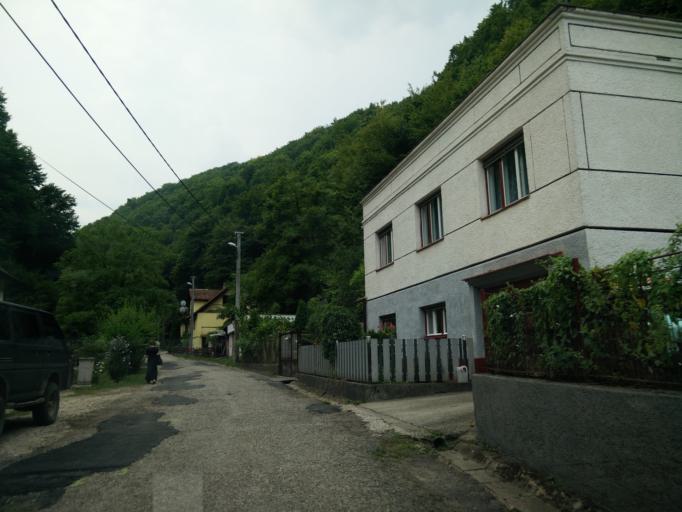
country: SK
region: Banskobystricky
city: Ziar nad Hronom
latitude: 48.5730
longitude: 18.8965
